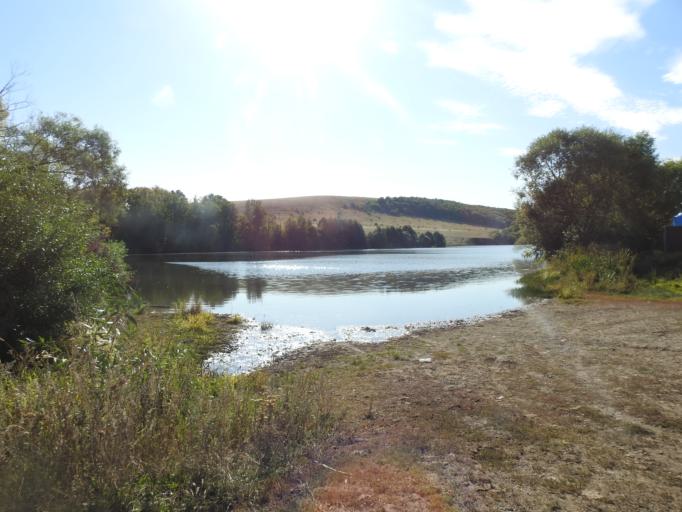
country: RU
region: Saratov
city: Novyye Burasy
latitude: 52.1442
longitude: 46.2557
